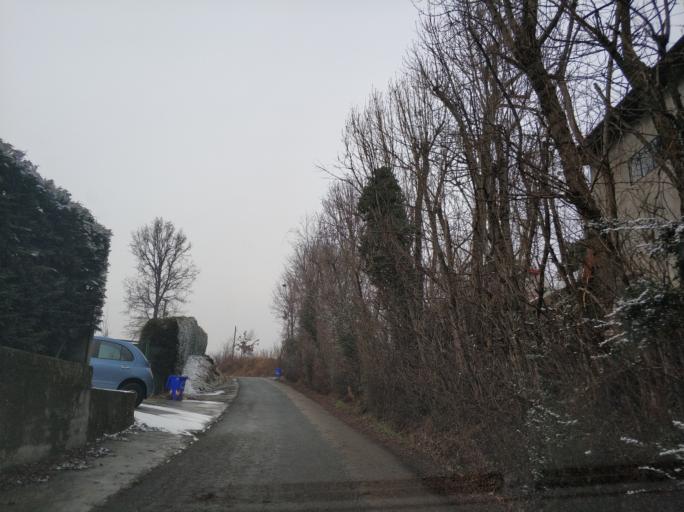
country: IT
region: Piedmont
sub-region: Provincia di Torino
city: San Francesco al Campo
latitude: 45.2175
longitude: 7.6787
